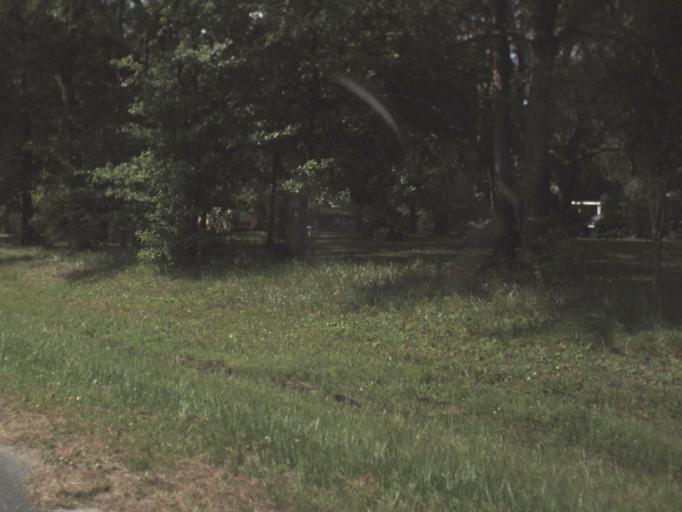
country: US
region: Florida
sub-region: Baker County
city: Macclenny
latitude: 30.3584
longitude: -82.1321
